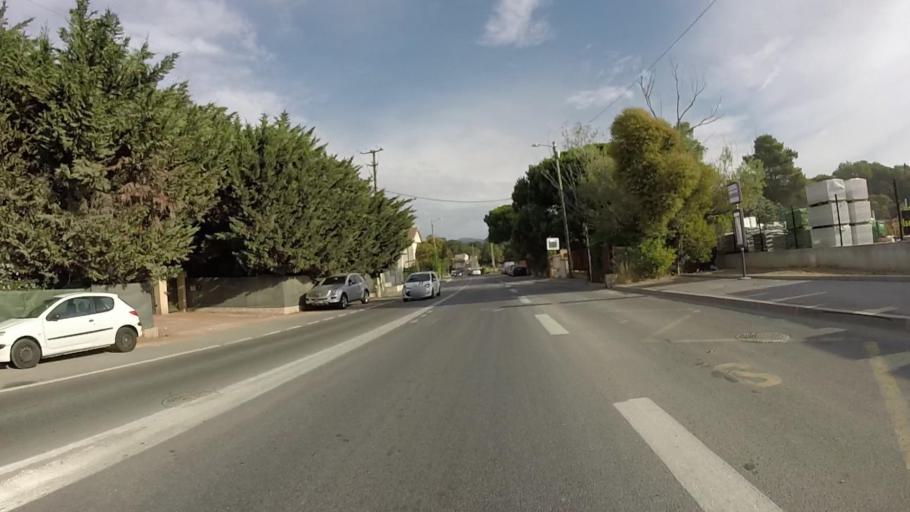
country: FR
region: Provence-Alpes-Cote d'Azur
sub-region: Departement des Alpes-Maritimes
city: Biot
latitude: 43.6080
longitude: 7.1113
